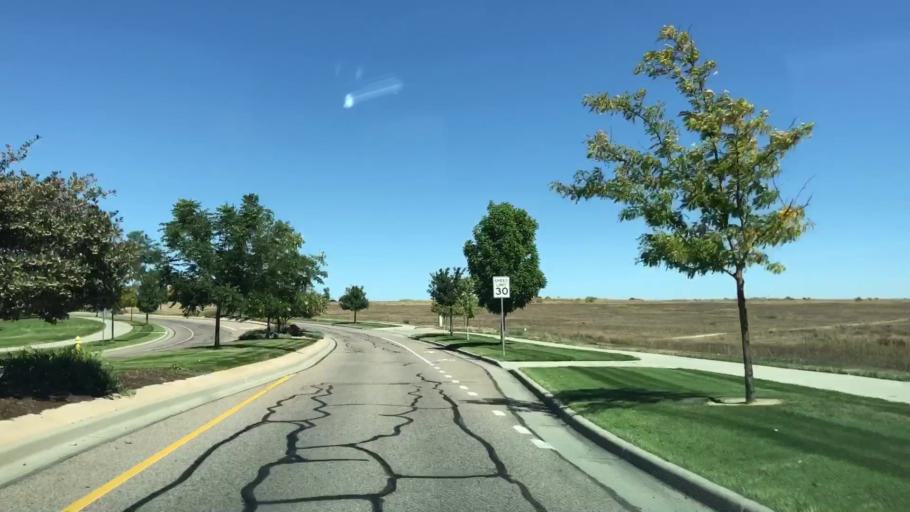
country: US
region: Colorado
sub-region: Weld County
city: Windsor
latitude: 40.5247
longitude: -104.9540
